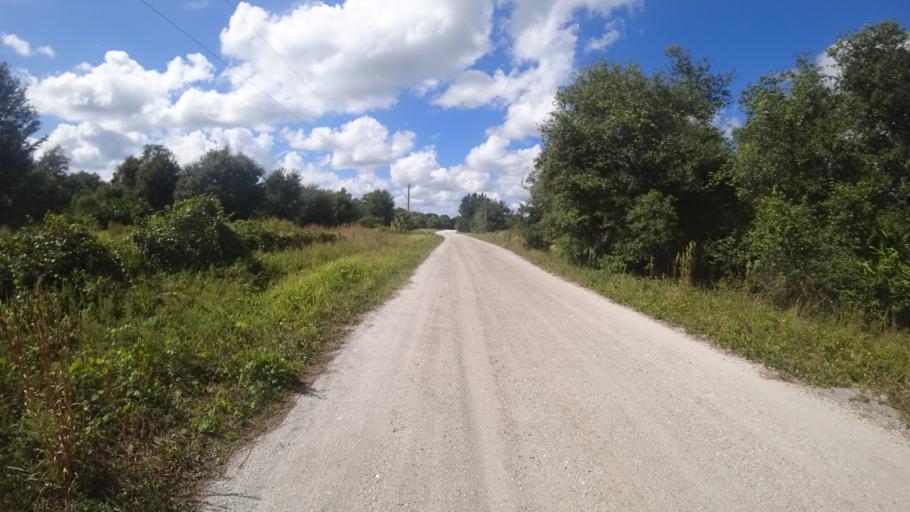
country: US
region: Florida
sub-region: Sarasota County
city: Lake Sarasota
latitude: 27.3204
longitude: -82.2562
